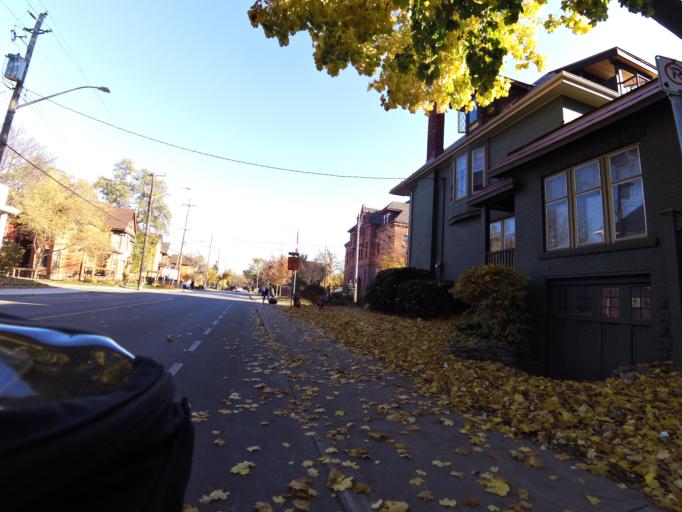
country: CA
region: Ontario
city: Hamilton
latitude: 43.2477
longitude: -79.8533
